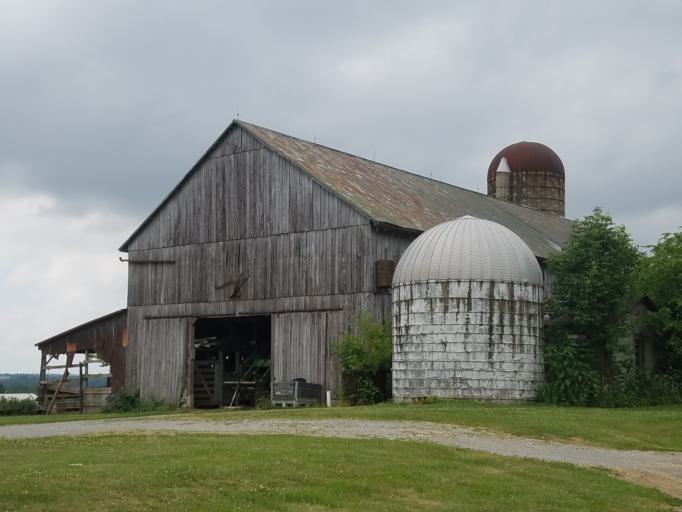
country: US
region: Kentucky
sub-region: Washington County
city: Springfield
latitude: 37.7679
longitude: -85.2081
